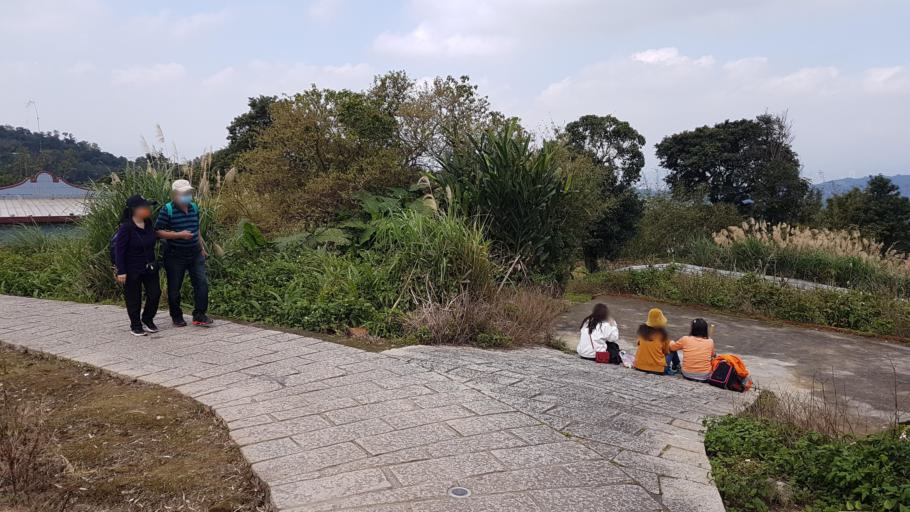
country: TW
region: Taipei
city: Taipei
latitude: 24.9676
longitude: 121.5871
